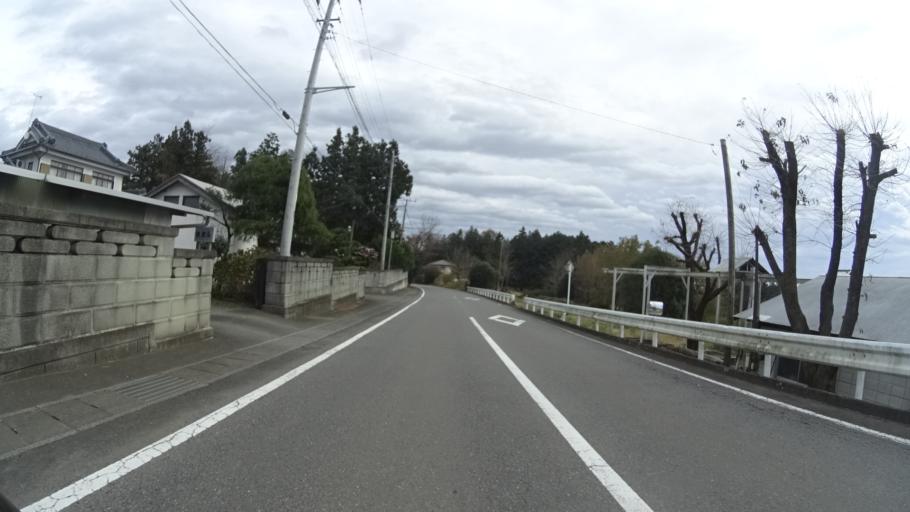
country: JP
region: Gunma
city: Maebashi-shi
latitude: 36.4735
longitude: 139.1350
